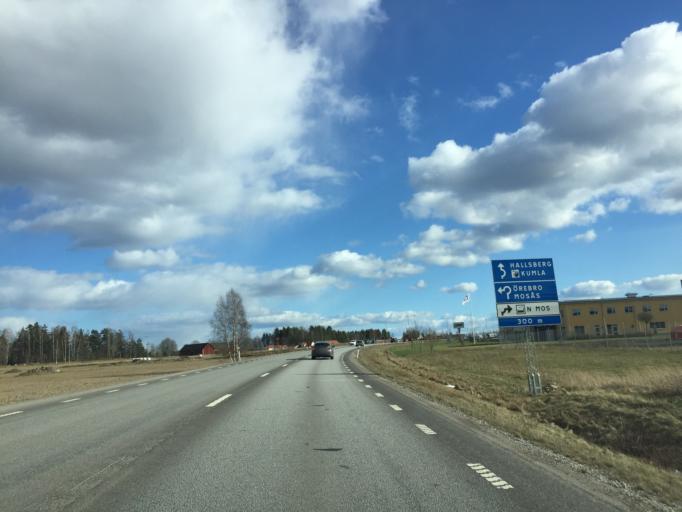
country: SE
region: OErebro
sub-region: Kumla Kommun
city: Kumla
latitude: 59.1538
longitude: 15.1382
